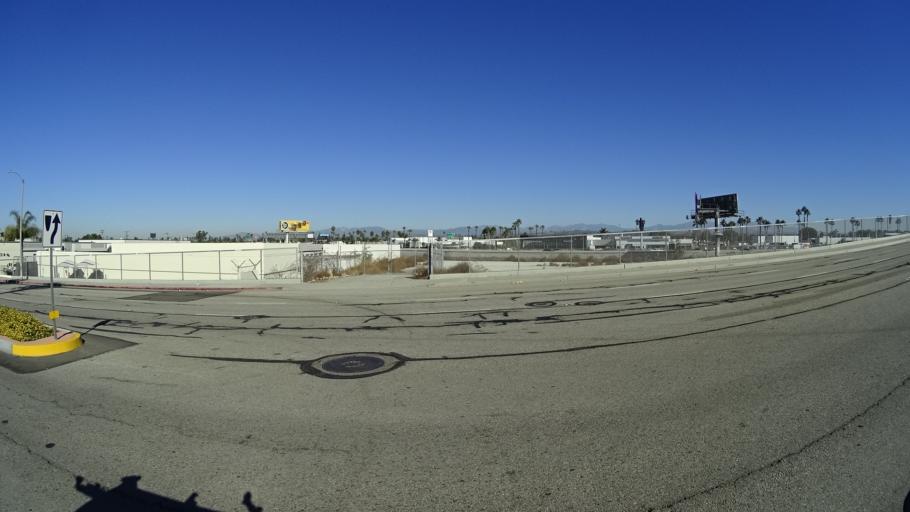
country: US
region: California
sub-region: Orange County
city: Buena Park
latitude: 33.8588
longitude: -117.9886
